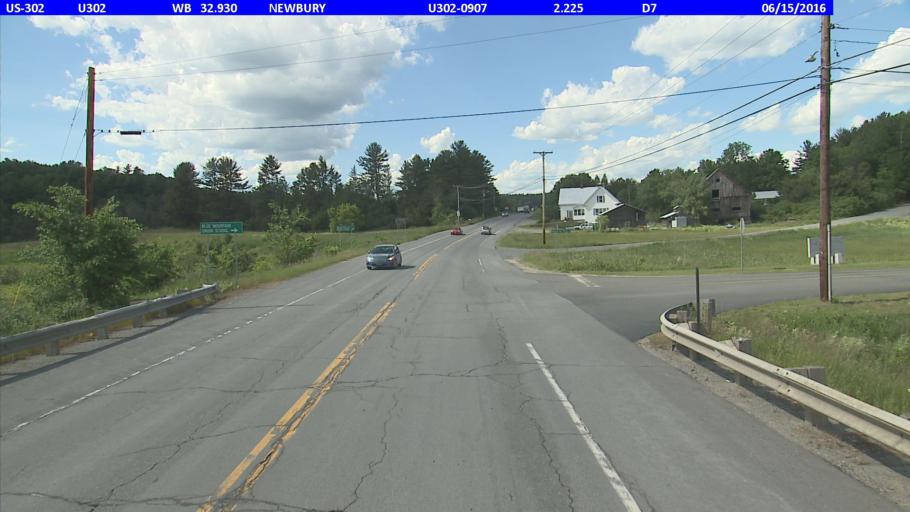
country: US
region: New Hampshire
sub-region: Grafton County
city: Woodsville
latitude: 44.1552
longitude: -72.0875
